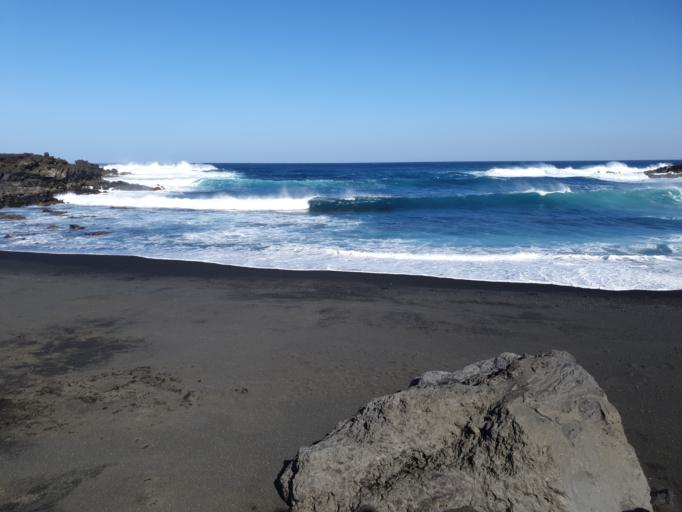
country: ES
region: Canary Islands
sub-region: Provincia de Las Palmas
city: Tinajo
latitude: 29.0636
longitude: -13.7672
